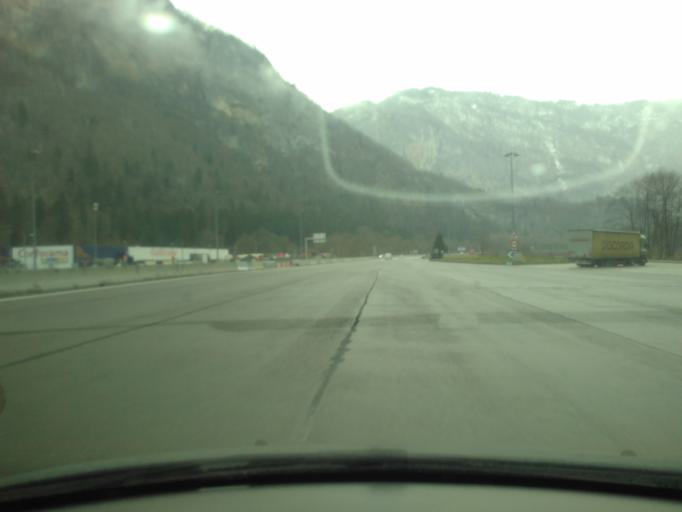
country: FR
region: Rhone-Alpes
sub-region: Departement de la Haute-Savoie
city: Cluses
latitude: 46.0465
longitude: 6.5977
